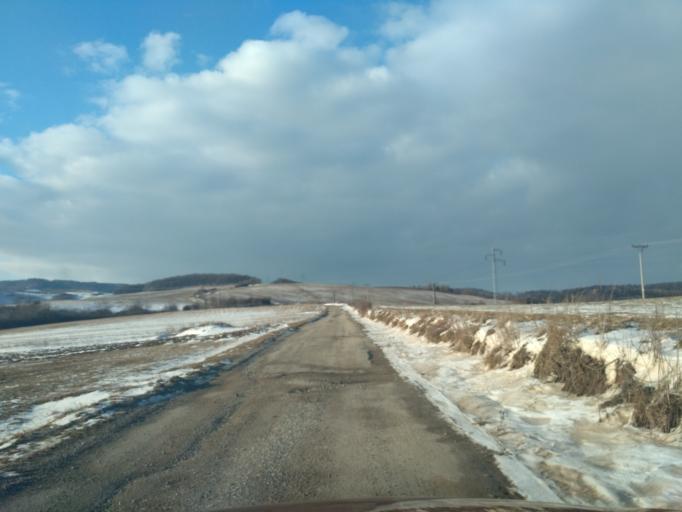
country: SK
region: Kosicky
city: Kosice
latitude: 48.7304
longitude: 21.1474
